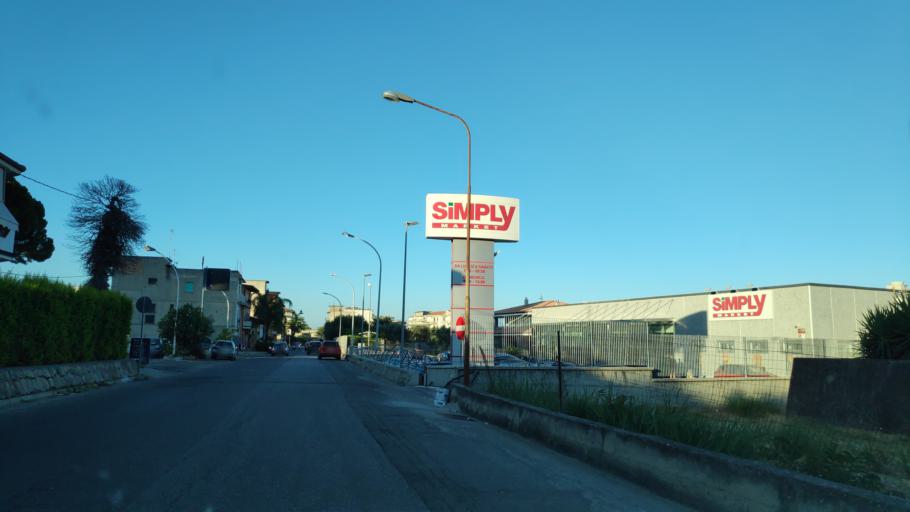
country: IT
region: Calabria
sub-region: Provincia di Reggio Calabria
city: Locri
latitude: 38.2374
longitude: 16.2505
